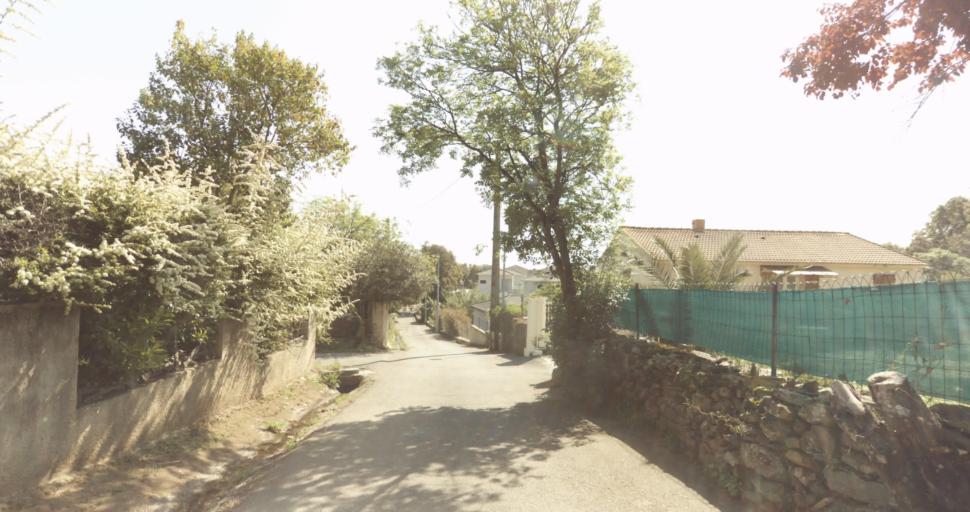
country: FR
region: Corsica
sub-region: Departement de la Haute-Corse
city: Biguglia
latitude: 42.6280
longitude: 9.4254
